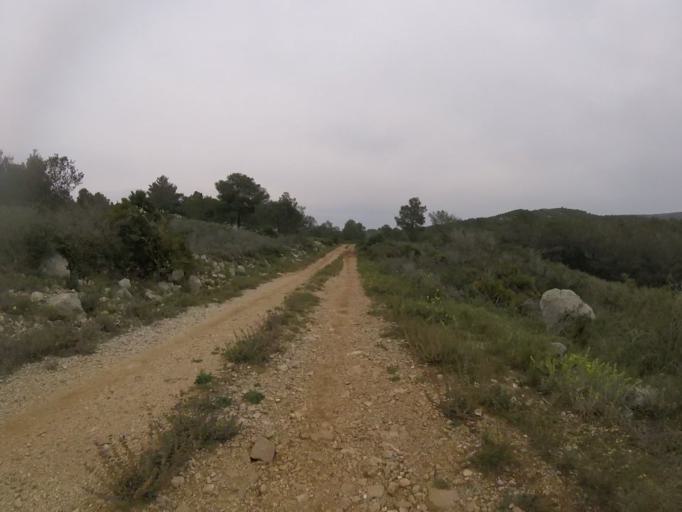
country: ES
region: Valencia
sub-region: Provincia de Castello
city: Alcala de Xivert
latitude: 40.3192
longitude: 0.2731
